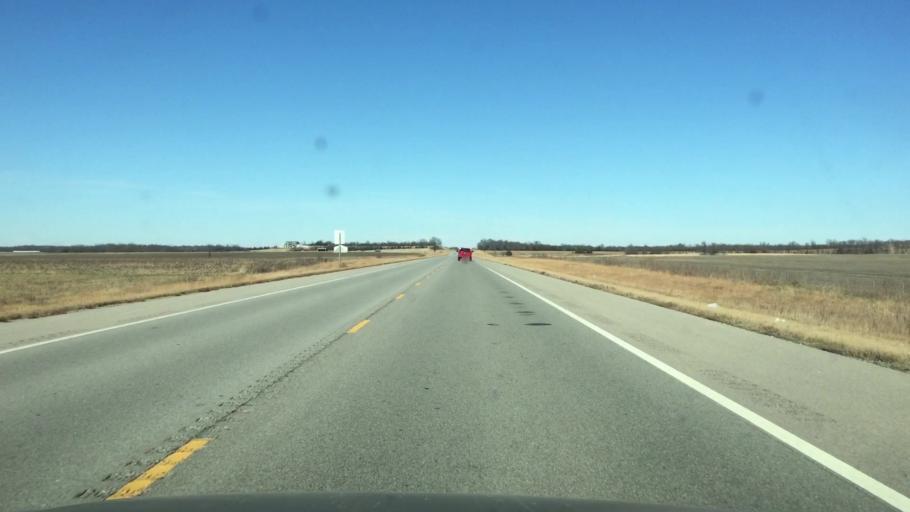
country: US
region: Kansas
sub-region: Allen County
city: Iola
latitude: 37.9586
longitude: -95.3812
